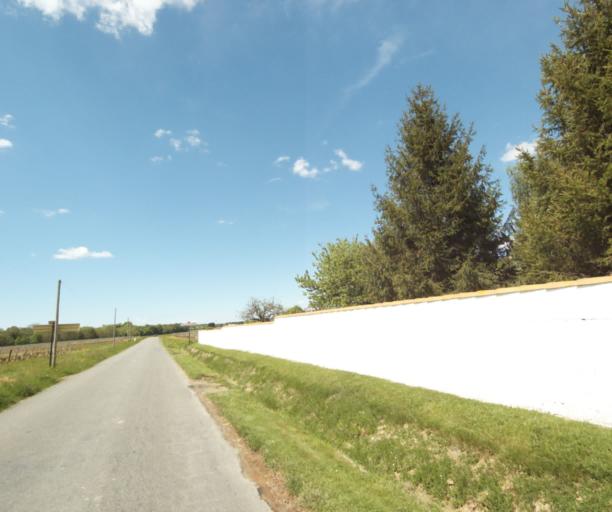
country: FR
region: Poitou-Charentes
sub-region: Departement de la Charente-Maritime
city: Burie
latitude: 45.7483
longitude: -0.4509
